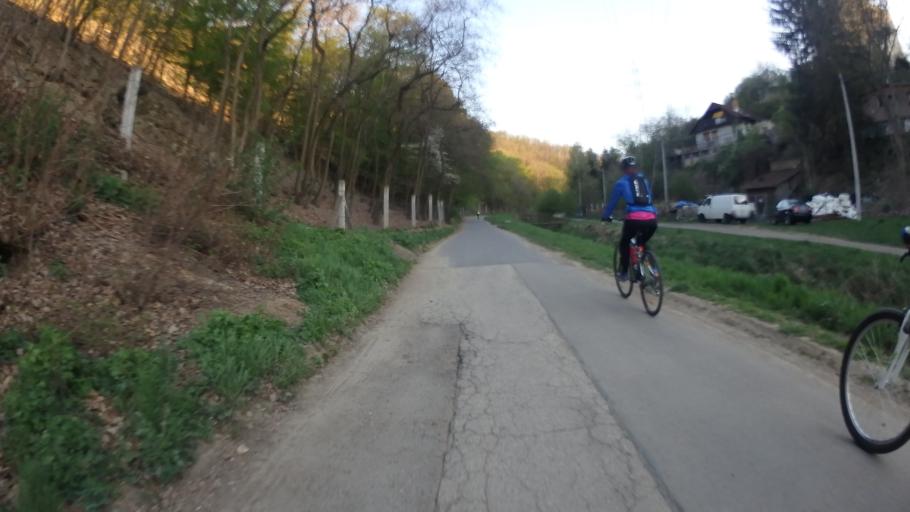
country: CZ
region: South Moravian
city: Troubsko
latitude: 49.2179
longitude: 16.5274
